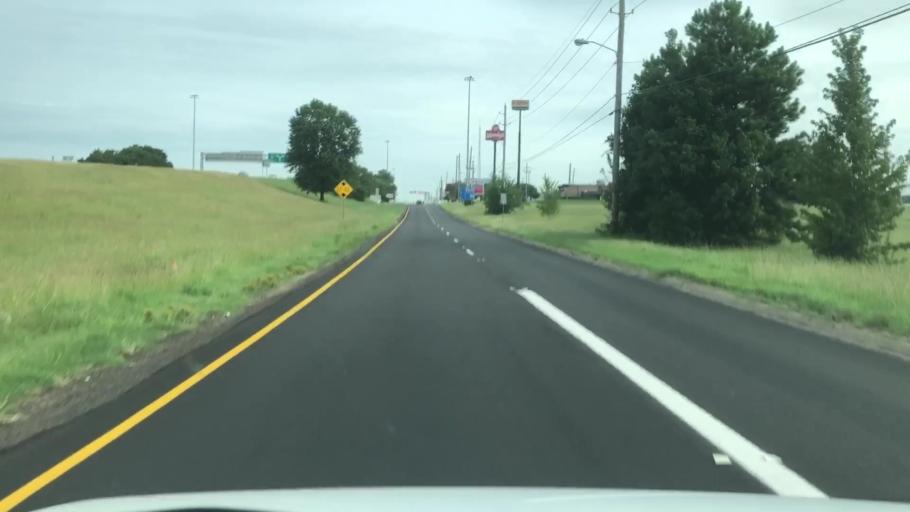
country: US
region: Texas
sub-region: Bowie County
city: Wake Village
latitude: 33.4404
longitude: -94.0962
